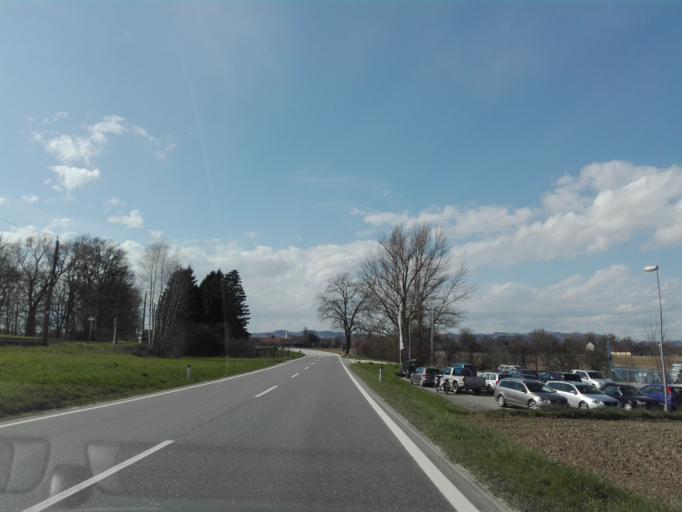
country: AT
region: Upper Austria
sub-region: Politischer Bezirk Urfahr-Umgebung
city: Feldkirchen an der Donau
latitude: 48.2900
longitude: 14.0557
